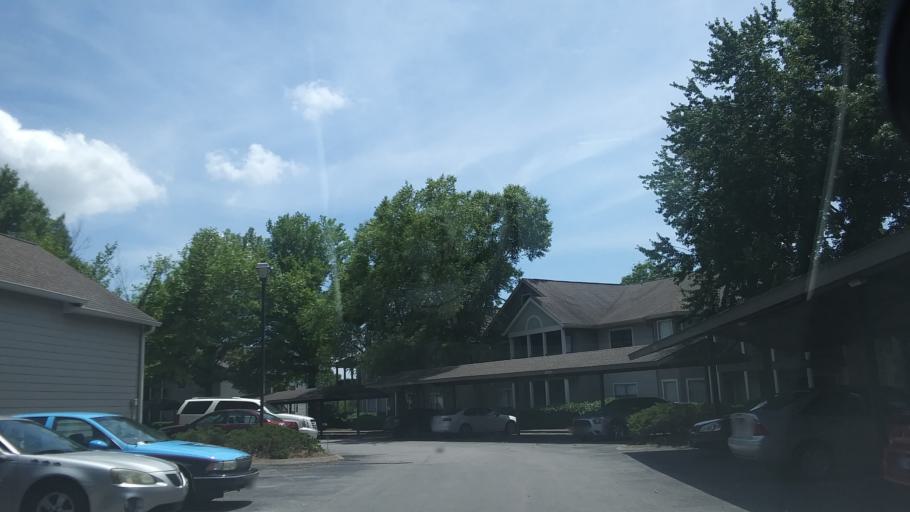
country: US
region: Tennessee
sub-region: Rutherford County
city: La Vergne
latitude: 36.0938
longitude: -86.6426
